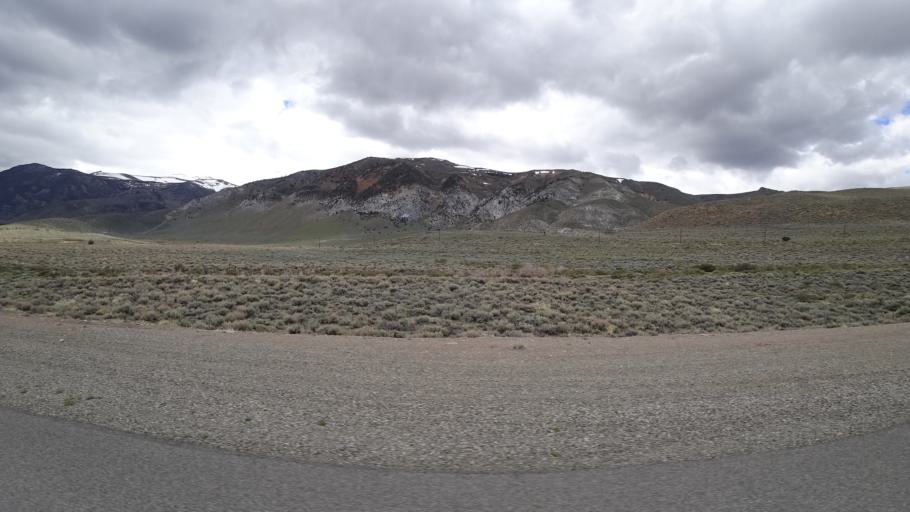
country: US
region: California
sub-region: Mono County
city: Bridgeport
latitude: 38.0543
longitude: -119.1656
